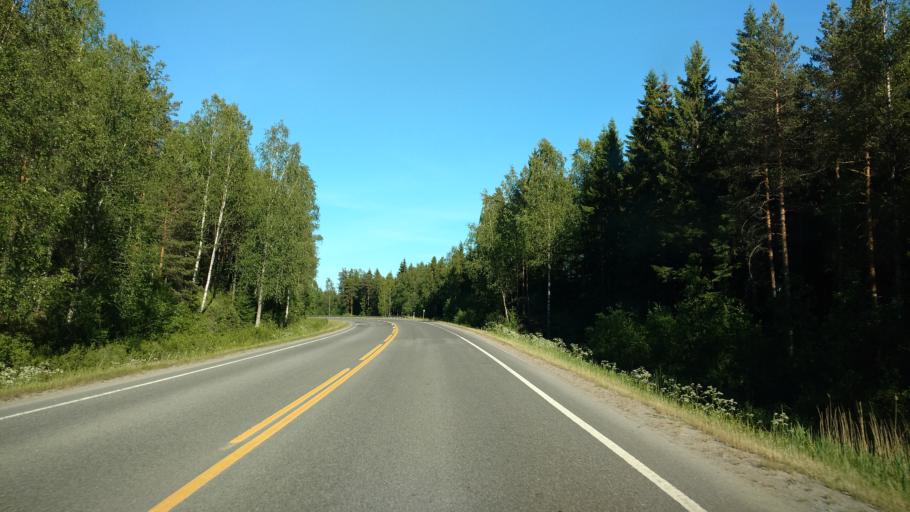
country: FI
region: Varsinais-Suomi
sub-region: Salo
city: Salo
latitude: 60.3816
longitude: 23.2056
